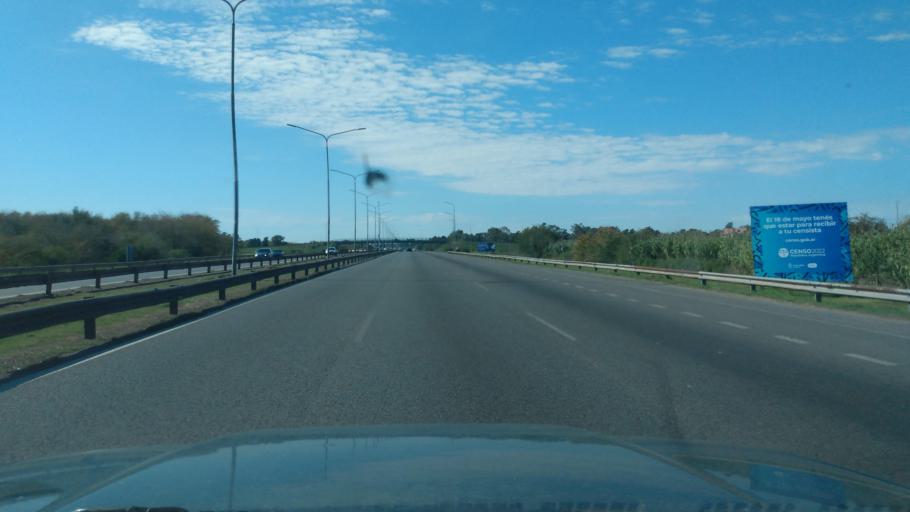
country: AR
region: Buenos Aires
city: Hurlingham
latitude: -34.5678
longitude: -58.6454
